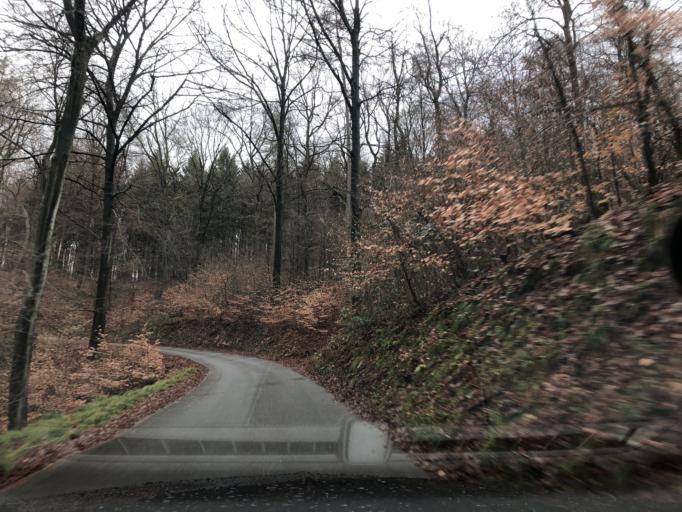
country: DE
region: Baden-Wuerttemberg
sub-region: Karlsruhe Region
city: Dossenheim
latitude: 49.4492
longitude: 8.6894
